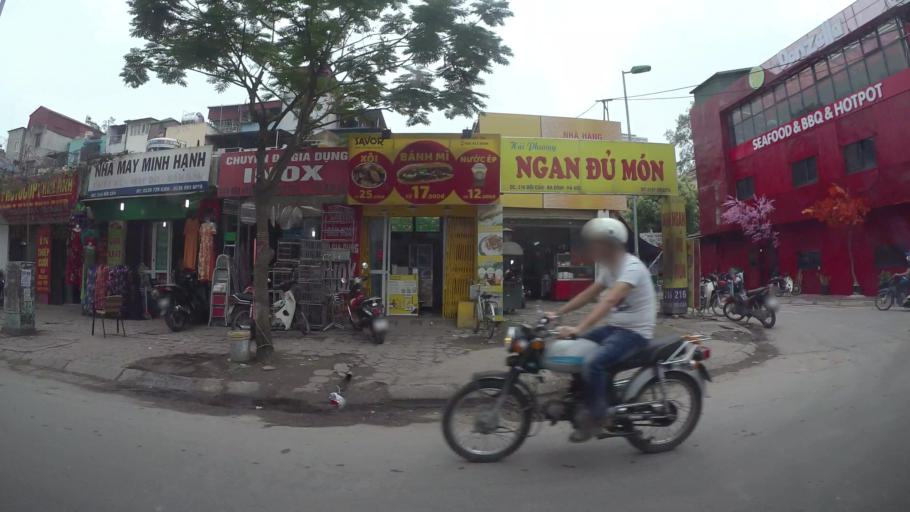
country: VN
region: Ha Noi
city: Dong Da
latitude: 21.0354
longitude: 105.8204
